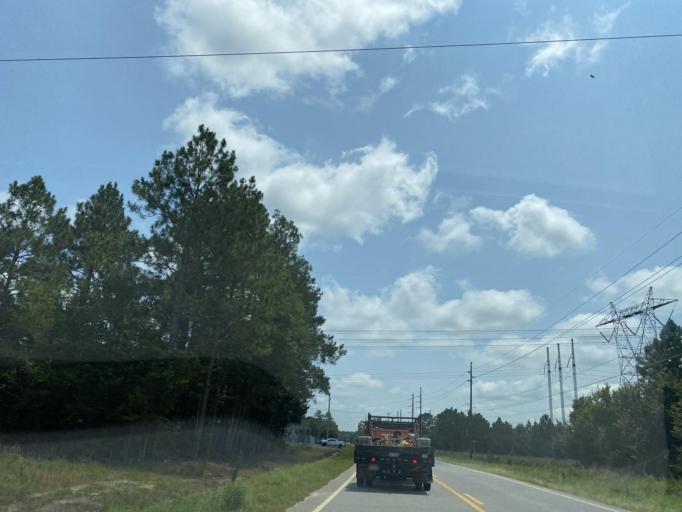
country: US
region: Georgia
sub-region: Jeff Davis County
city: Hazlehurst
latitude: 31.8129
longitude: -82.5674
